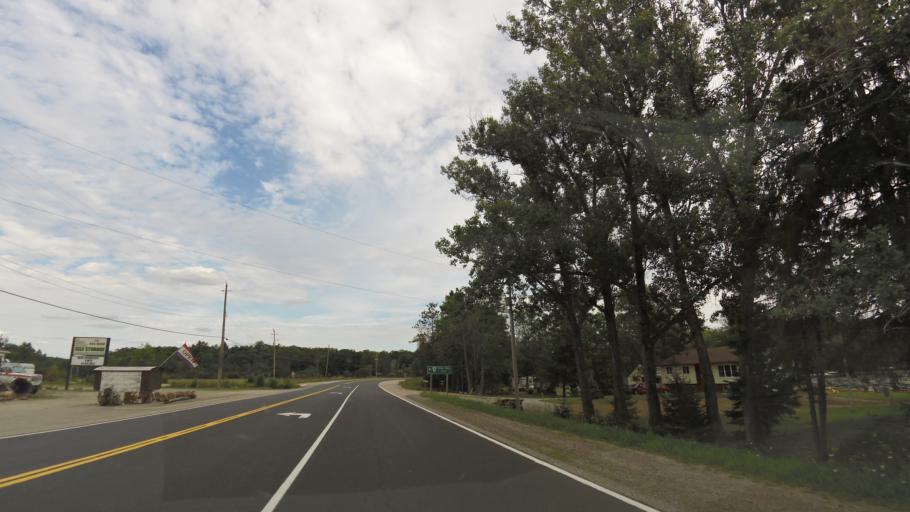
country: CA
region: Ontario
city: Bracebridge
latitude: 44.8068
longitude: -78.8089
